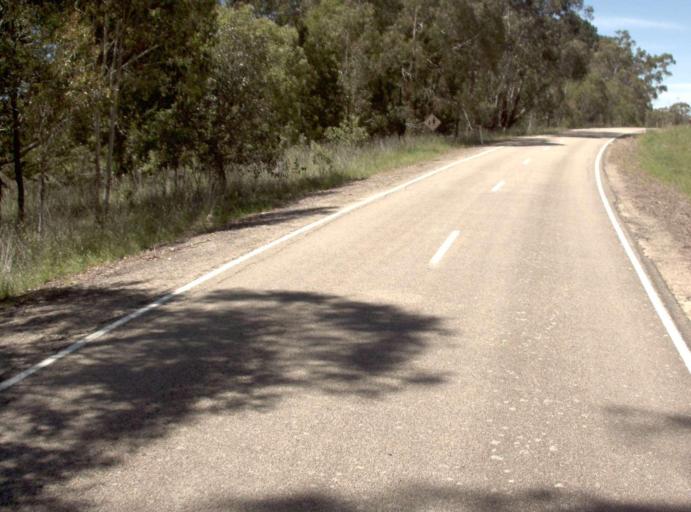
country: AU
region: Victoria
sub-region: East Gippsland
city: Lakes Entrance
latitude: -37.1580
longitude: 148.2586
